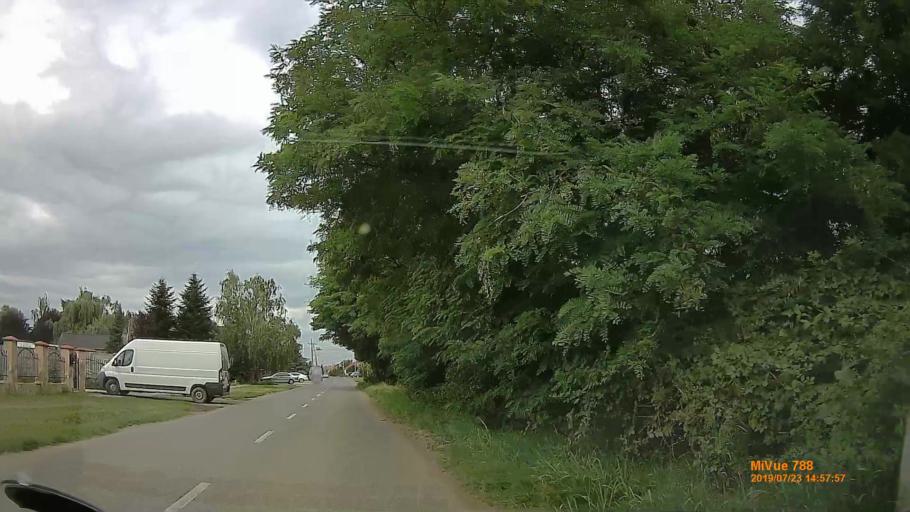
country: HU
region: Szabolcs-Szatmar-Bereg
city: Nyiregyhaza
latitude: 47.9097
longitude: 21.6740
